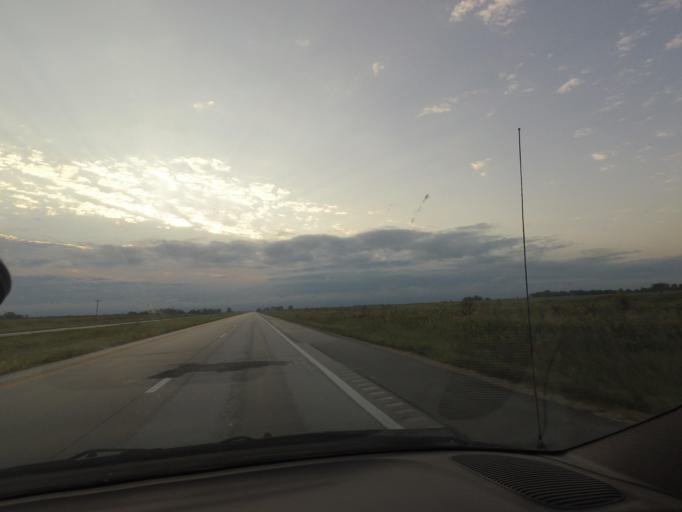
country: US
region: Missouri
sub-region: Shelby County
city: Shelbina
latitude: 39.7136
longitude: -92.1252
